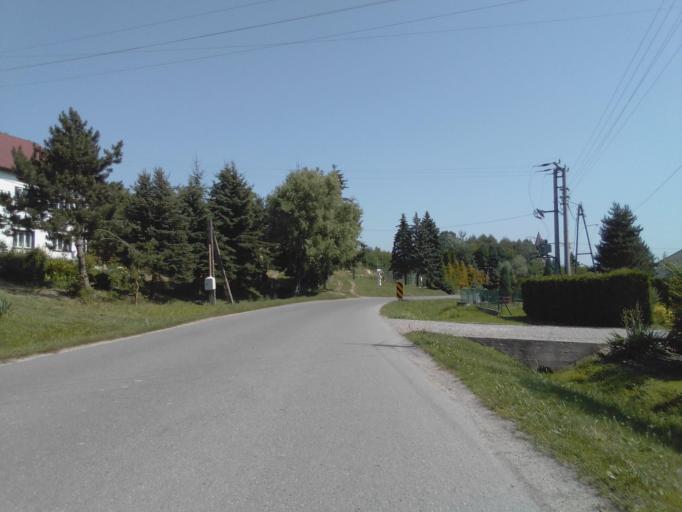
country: PL
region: Subcarpathian Voivodeship
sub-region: Powiat ropczycko-sedziszowski
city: Zagorzyce
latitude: 50.0430
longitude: 21.6557
